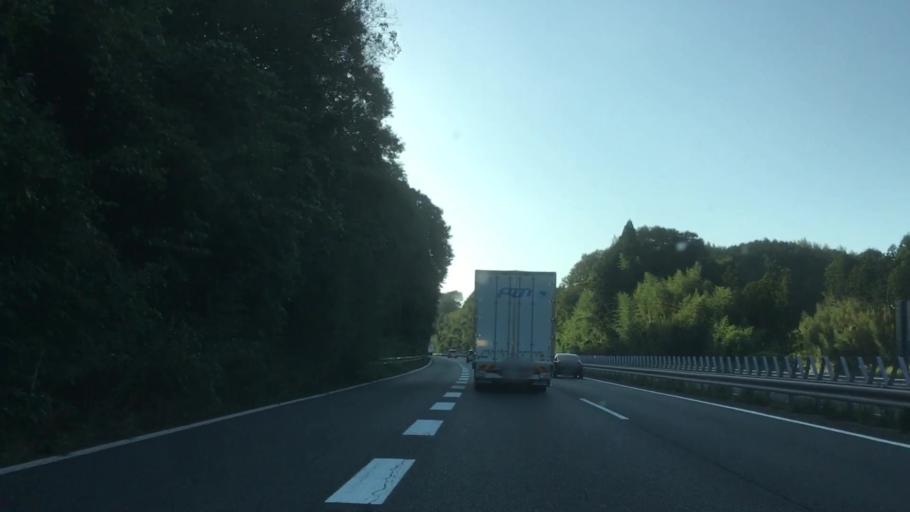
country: JP
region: Yamaguchi
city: Onoda
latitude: 34.1171
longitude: 131.1184
